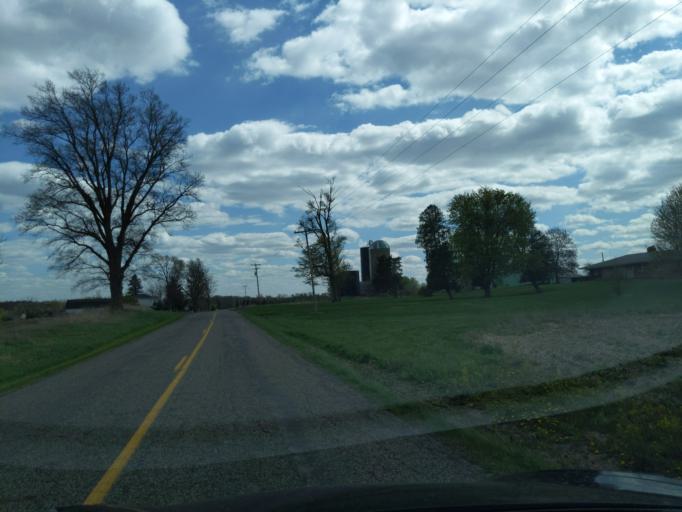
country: US
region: Michigan
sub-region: Ingham County
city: Leslie
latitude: 42.4719
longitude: -84.5412
